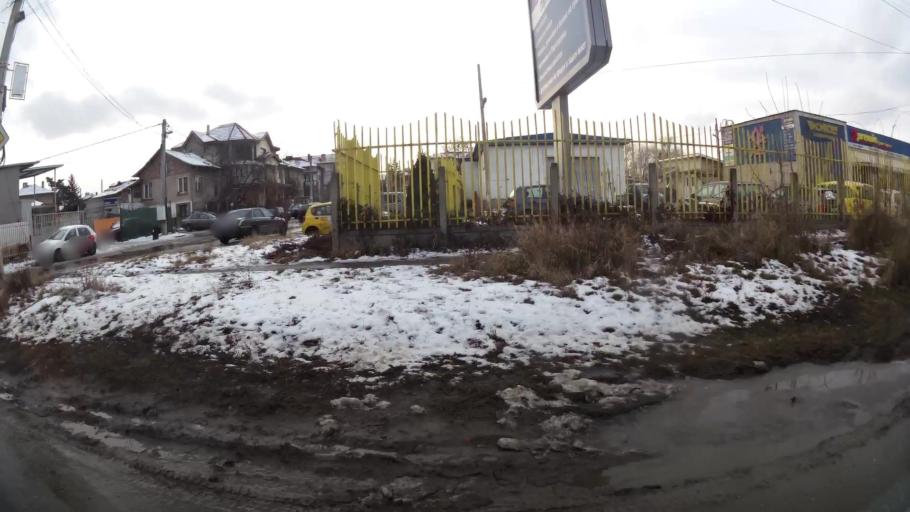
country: BG
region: Sofia-Capital
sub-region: Stolichna Obshtina
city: Sofia
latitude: 42.7291
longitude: 23.3442
